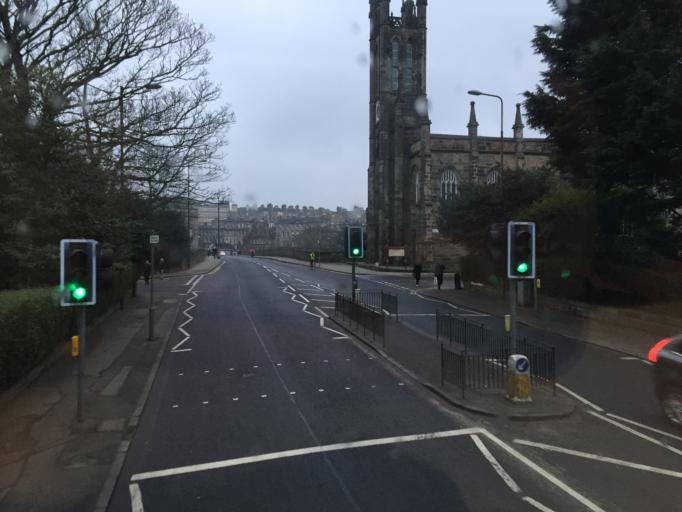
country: GB
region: Scotland
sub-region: Edinburgh
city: Edinburgh
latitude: 55.9542
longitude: -3.2151
